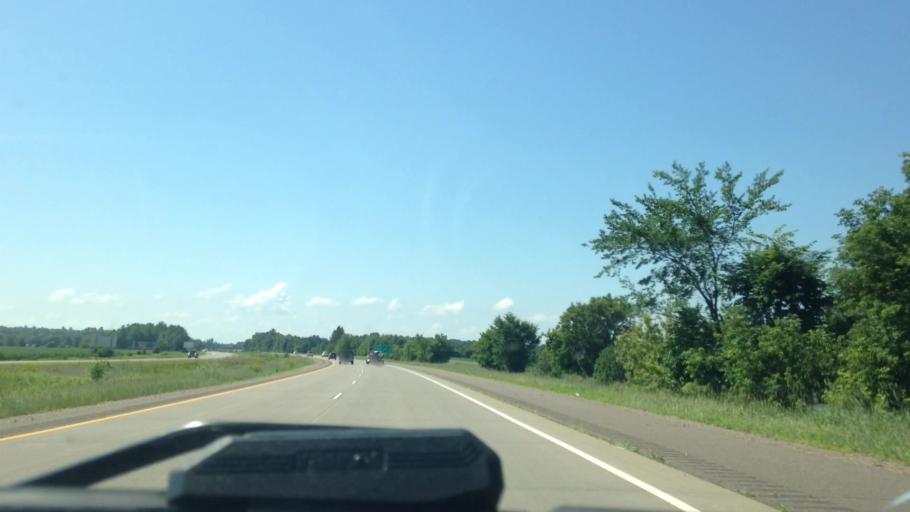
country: US
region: Wisconsin
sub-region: Barron County
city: Cameron
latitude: 45.4582
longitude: -91.7597
